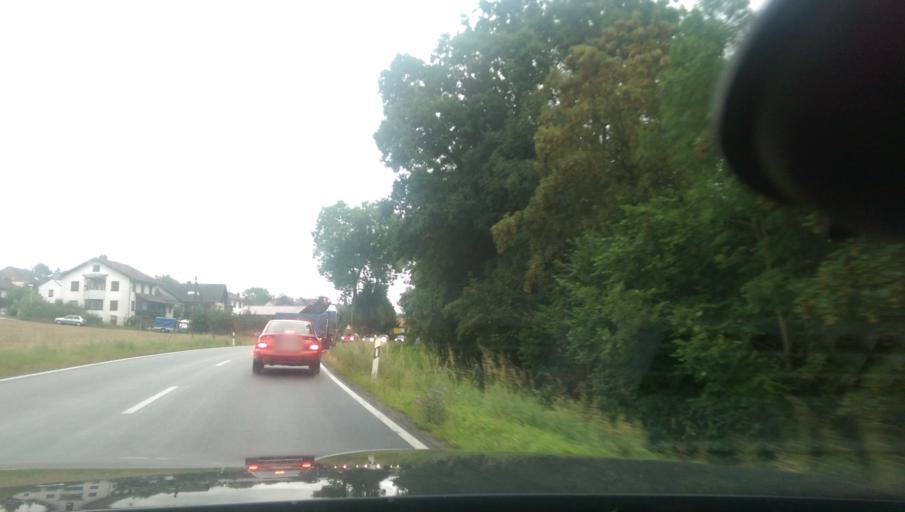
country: DE
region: Hesse
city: Witzenhausen
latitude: 51.2876
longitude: 9.8462
